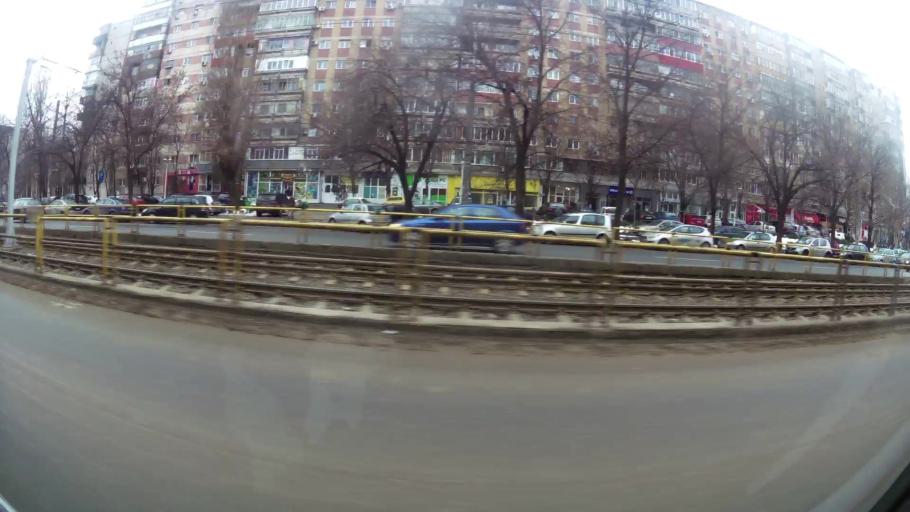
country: RO
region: Ilfov
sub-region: Comuna Chiajna
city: Rosu
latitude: 44.4169
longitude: 26.0343
